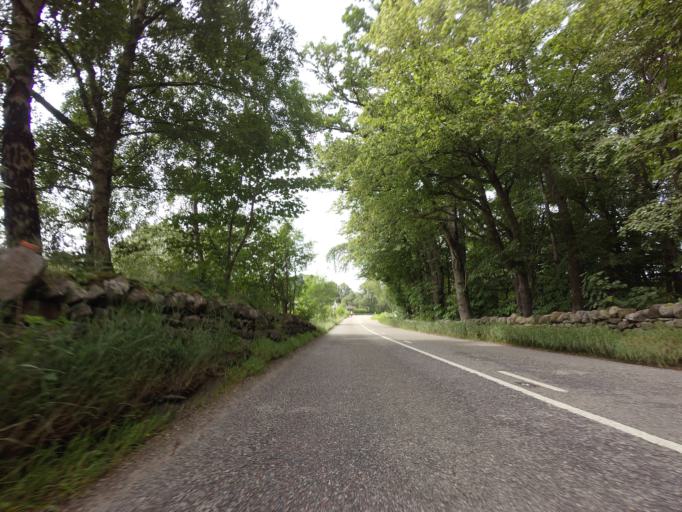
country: GB
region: Scotland
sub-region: Highland
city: Alness
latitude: 57.8560
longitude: -4.3101
